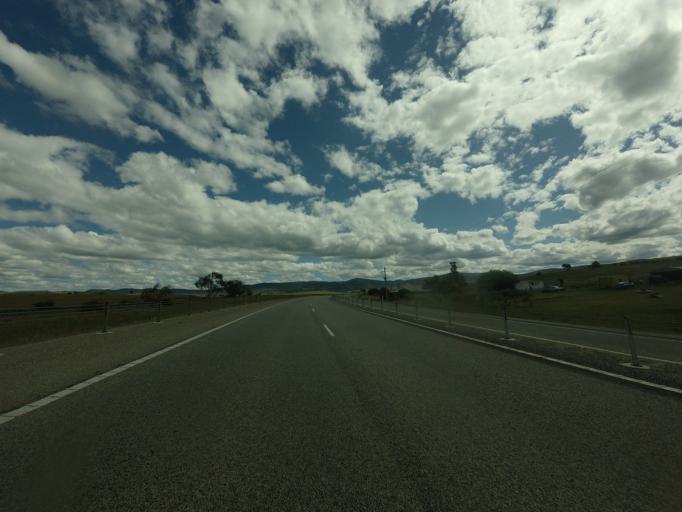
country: AU
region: Tasmania
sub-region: Northern Midlands
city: Evandale
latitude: -42.1479
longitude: 147.4157
